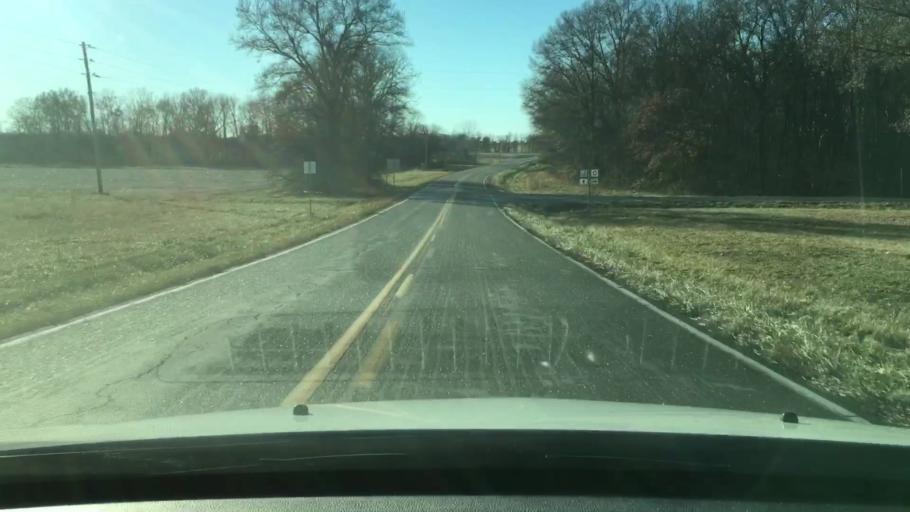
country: US
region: Missouri
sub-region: Audrain County
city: Mexico
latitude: 39.2801
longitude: -91.7701
